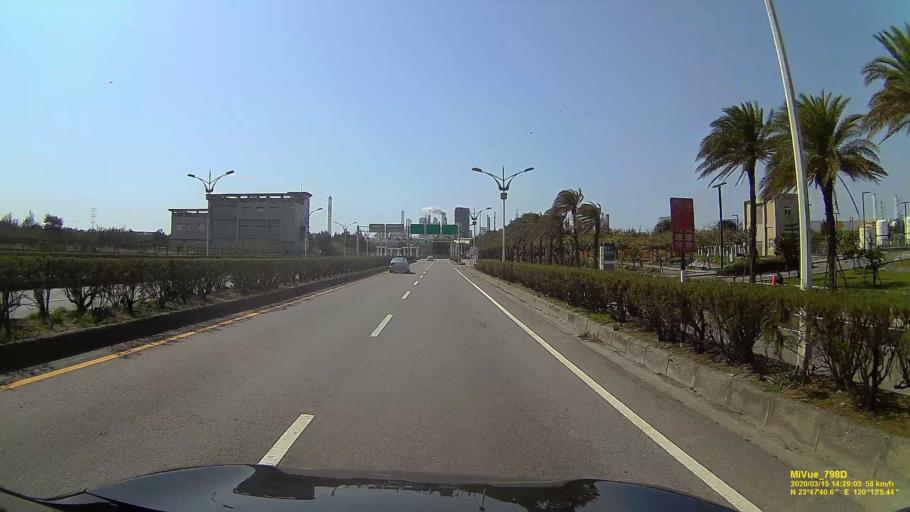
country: TW
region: Taiwan
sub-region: Yunlin
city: Douliu
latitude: 23.7948
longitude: 120.2177
